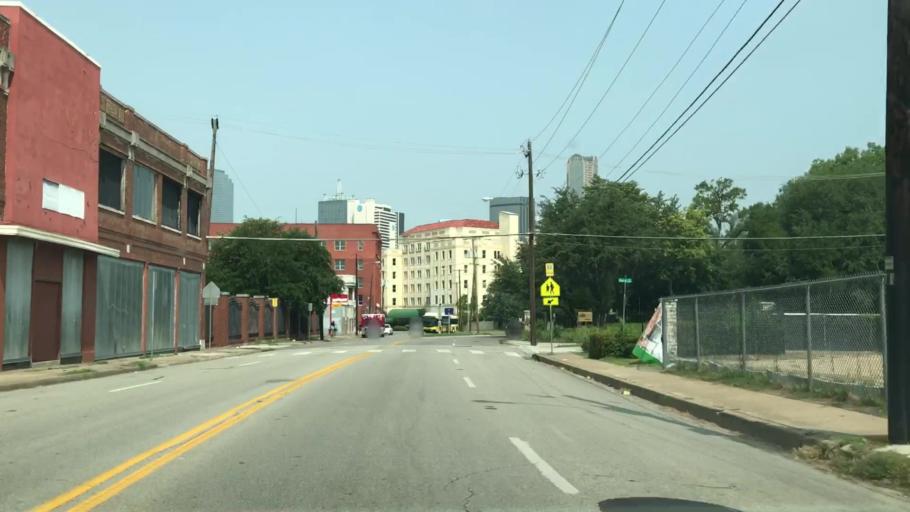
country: US
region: Texas
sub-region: Dallas County
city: Dallas
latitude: 32.7712
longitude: -96.7889
